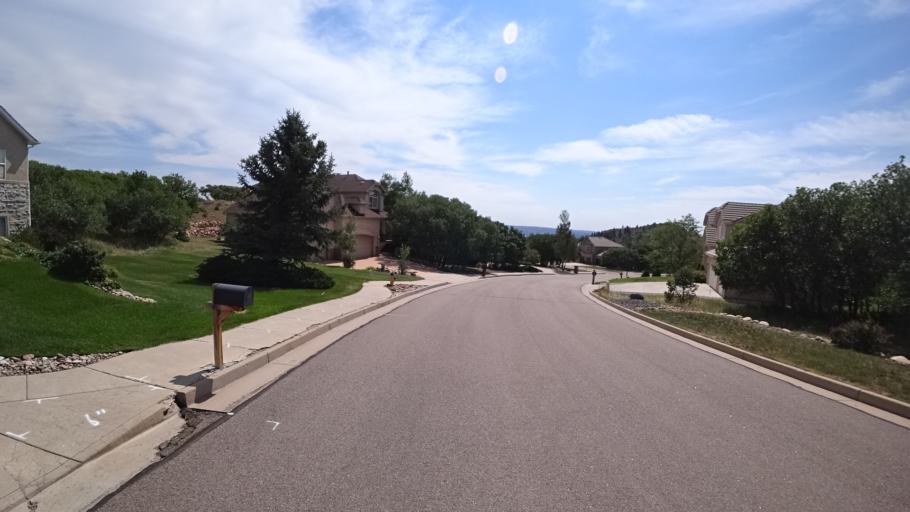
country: US
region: Colorado
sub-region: El Paso County
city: Air Force Academy
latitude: 38.9490
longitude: -104.8834
